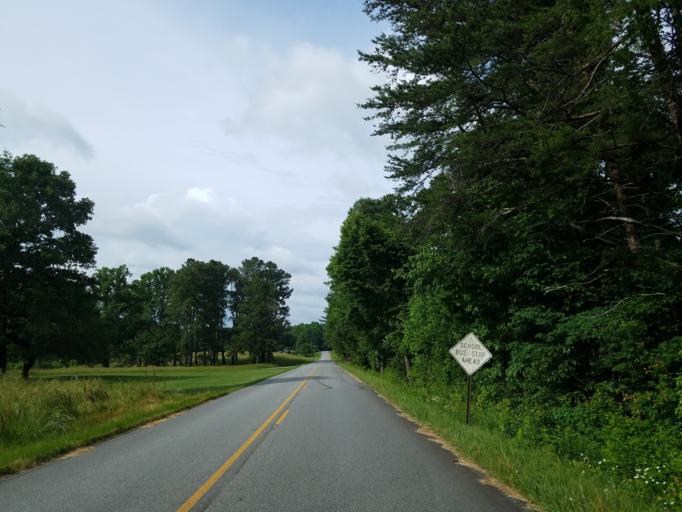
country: US
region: Georgia
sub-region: Dawson County
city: Dawsonville
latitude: 34.4778
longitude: -84.1753
